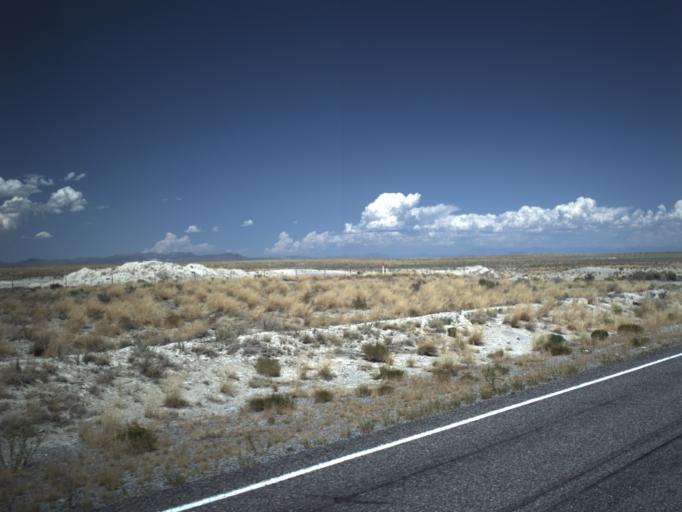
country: US
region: Utah
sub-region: Millard County
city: Delta
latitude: 39.1758
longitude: -113.0254
